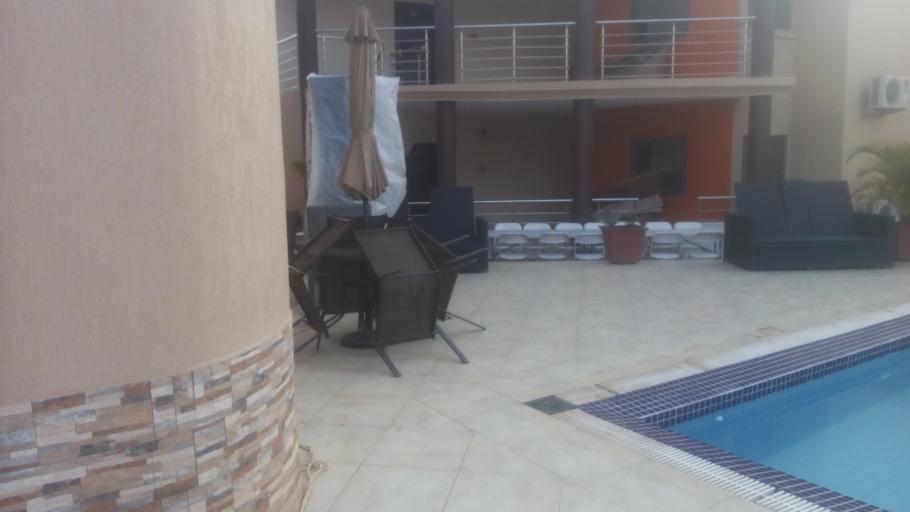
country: GH
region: Western
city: Tarkwa
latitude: 5.2375
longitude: -2.0118
